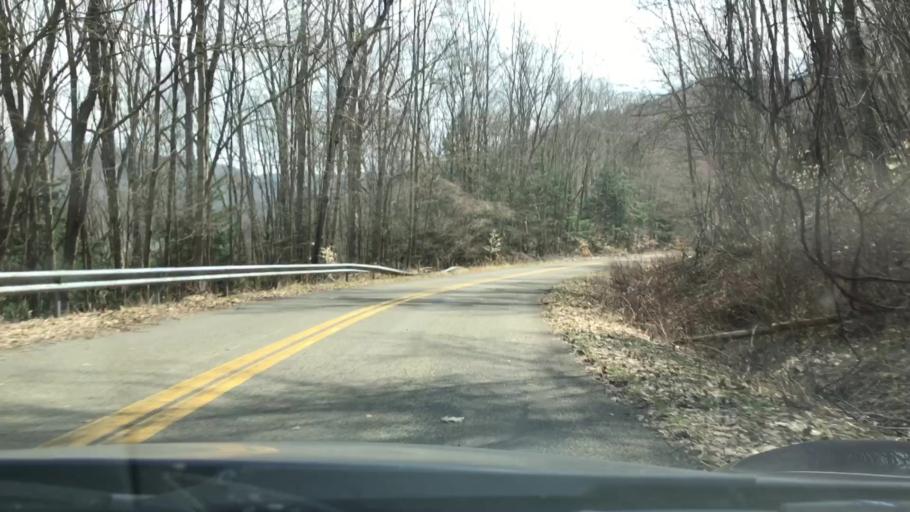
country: US
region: Pennsylvania
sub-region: Warren County
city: Sheffield
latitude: 41.8153
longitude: -78.9417
